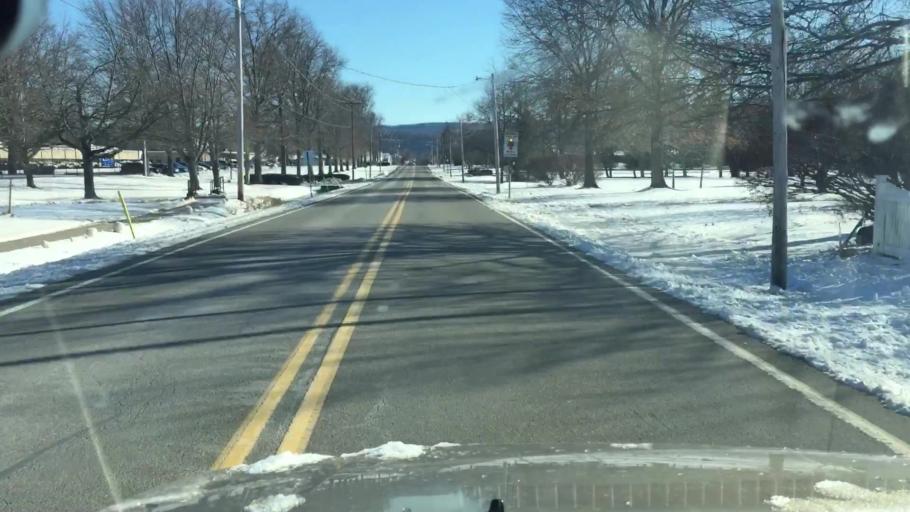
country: US
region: Pennsylvania
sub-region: Luzerne County
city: East Berwick
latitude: 41.0678
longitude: -76.2319
